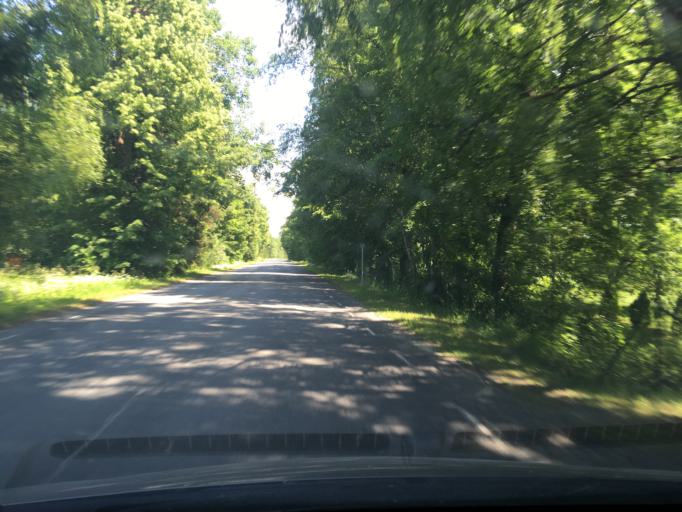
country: EE
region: Paernumaa
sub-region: Halinga vald
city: Parnu-Jaagupi
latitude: 58.7172
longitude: 24.3489
